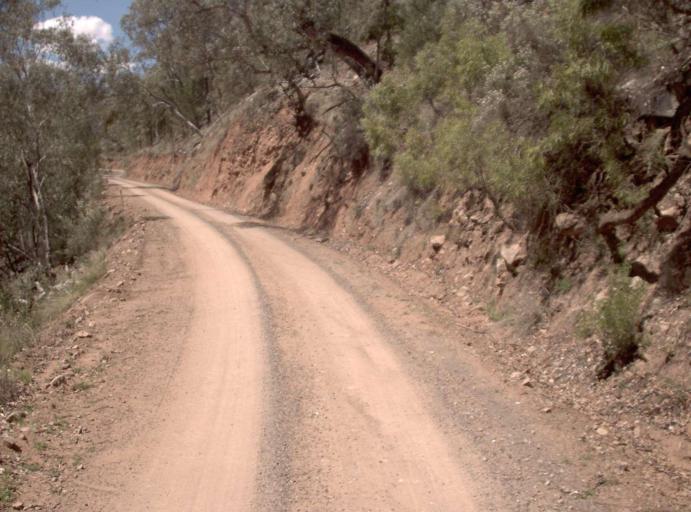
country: AU
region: New South Wales
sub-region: Snowy River
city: Jindabyne
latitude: -37.0573
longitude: 148.5330
